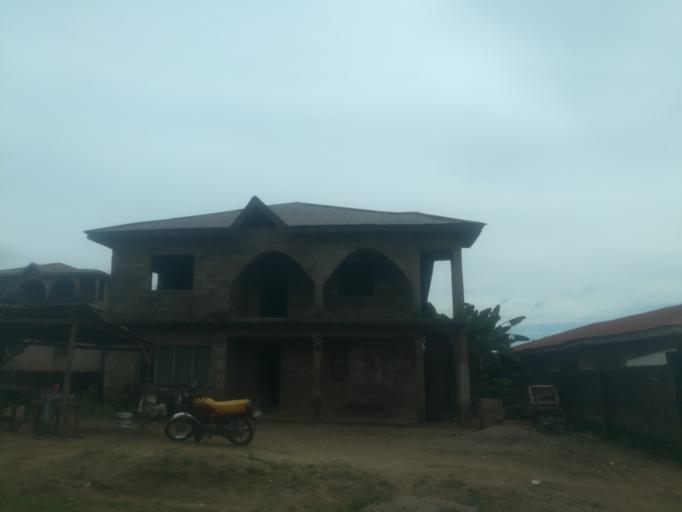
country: NG
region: Oyo
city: Ibadan
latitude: 7.3749
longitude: 3.9630
